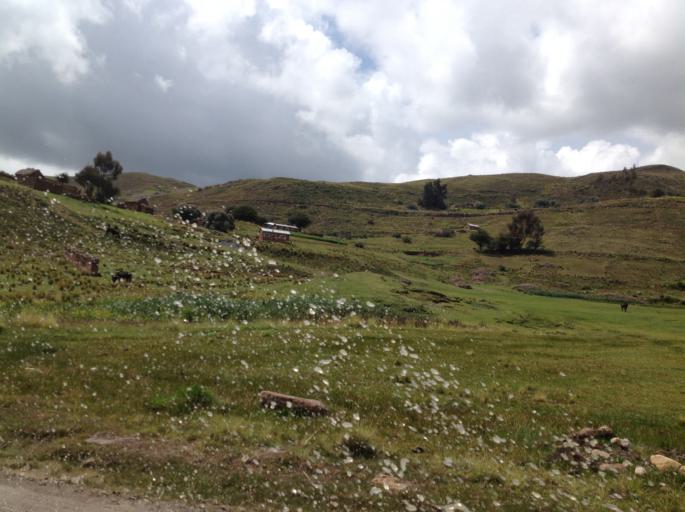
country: BO
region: La Paz
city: Yumani
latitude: -15.7728
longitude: -68.9992
